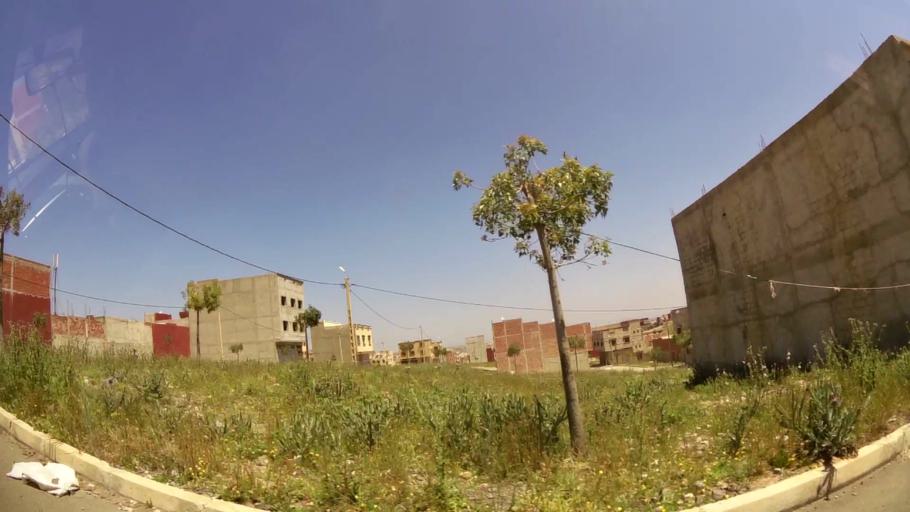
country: MA
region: Oriental
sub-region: Oujda-Angad
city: Oujda
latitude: 34.6756
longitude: -1.9523
